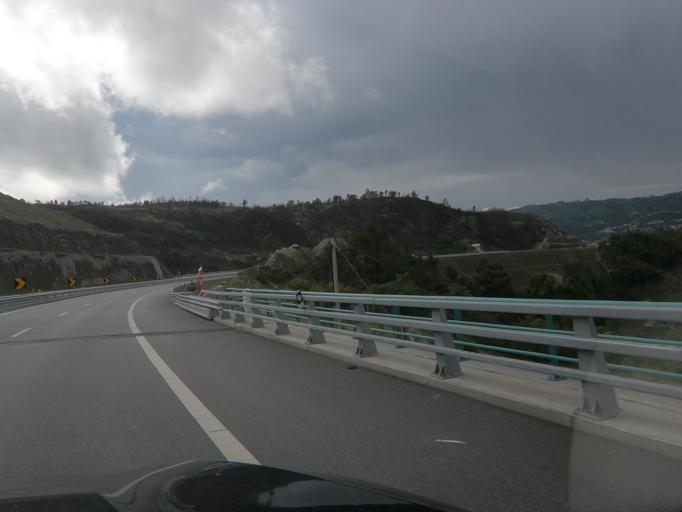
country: PT
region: Porto
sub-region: Amarante
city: Amarante
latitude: 41.2487
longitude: -7.9933
